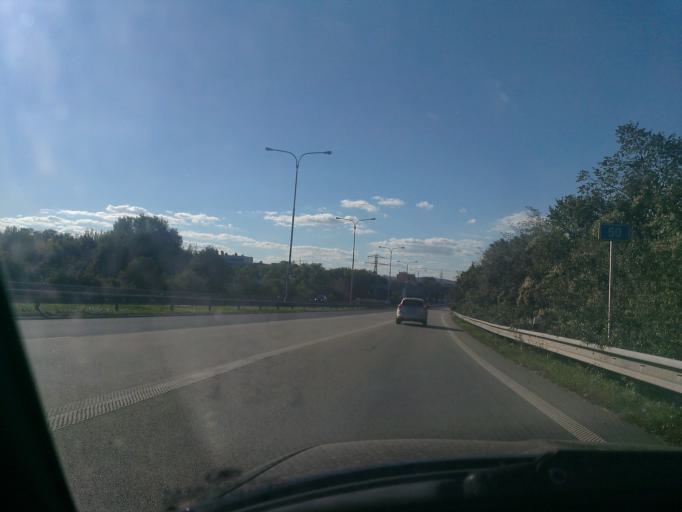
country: CZ
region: South Moravian
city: Podoli
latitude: 49.1859
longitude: 16.6659
